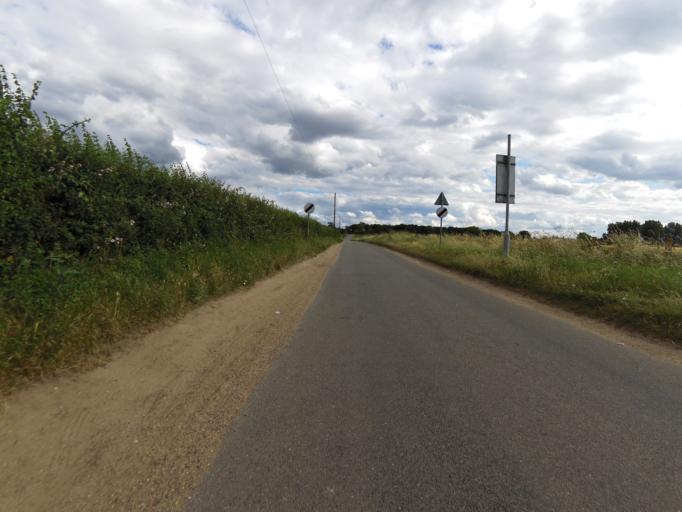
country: GB
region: England
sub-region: Norfolk
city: Ditchingham
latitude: 52.4776
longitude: 1.4818
